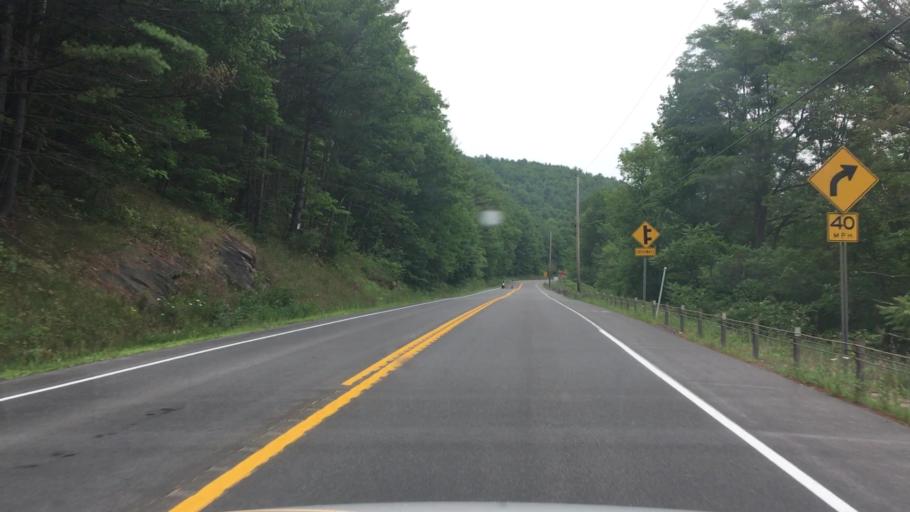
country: US
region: New York
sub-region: Essex County
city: Keeseville
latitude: 44.4735
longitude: -73.5702
